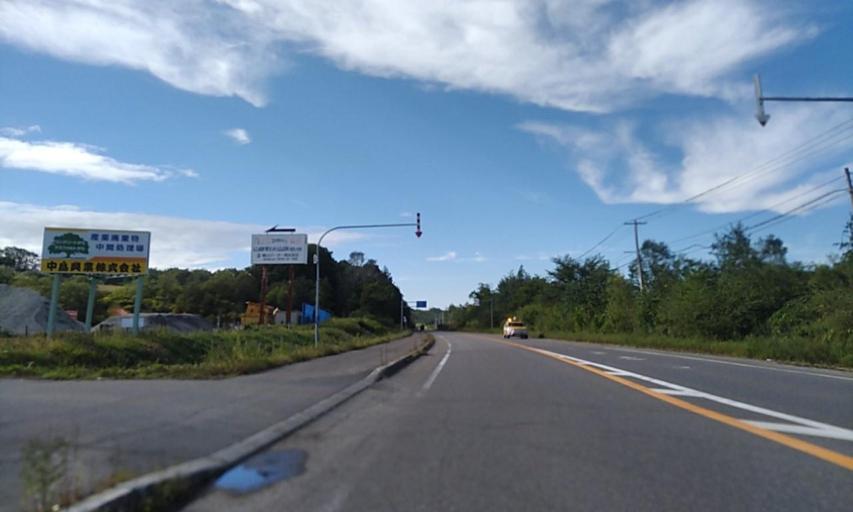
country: JP
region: Hokkaido
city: Obihiro
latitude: 42.8170
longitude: 143.4876
